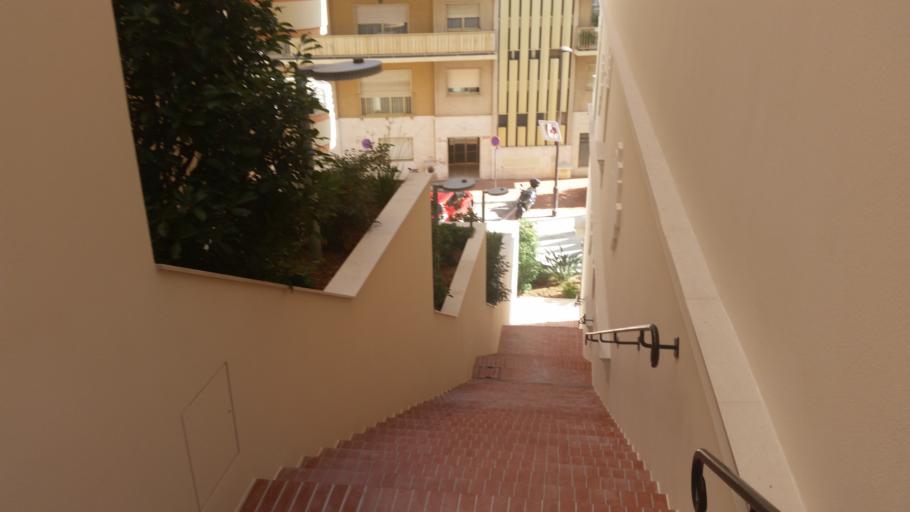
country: MC
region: Commune de Monaco
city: Monaco
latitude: 43.7326
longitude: 7.4152
